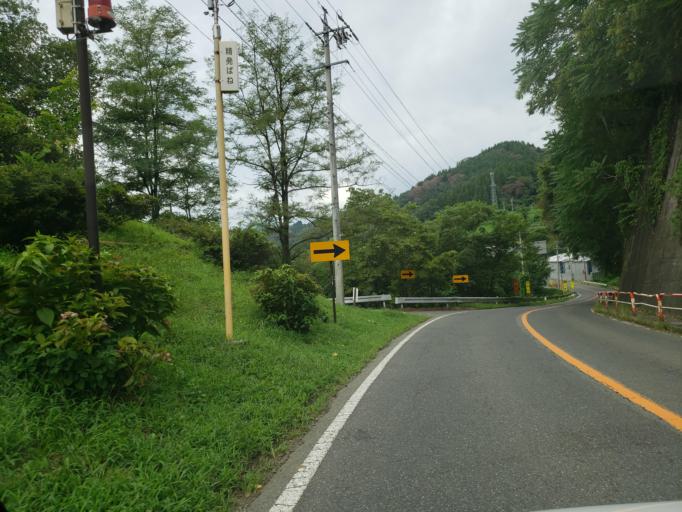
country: JP
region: Nagano
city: Nagano-shi
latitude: 36.6126
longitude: 138.0574
